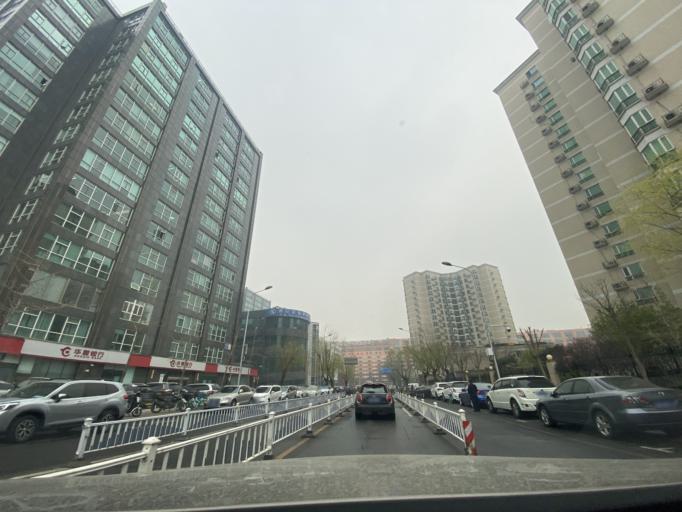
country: CN
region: Beijing
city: Sijiqing
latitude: 39.9602
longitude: 116.2813
